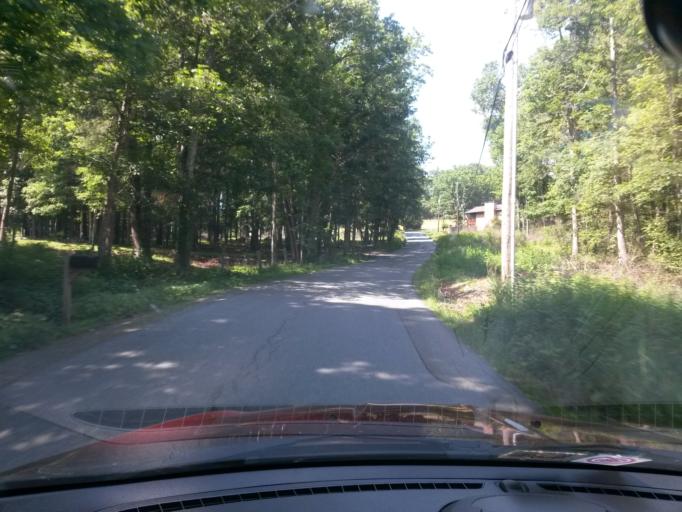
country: US
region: West Virginia
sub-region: Mercer County
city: Princeton
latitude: 37.3951
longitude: -81.1134
